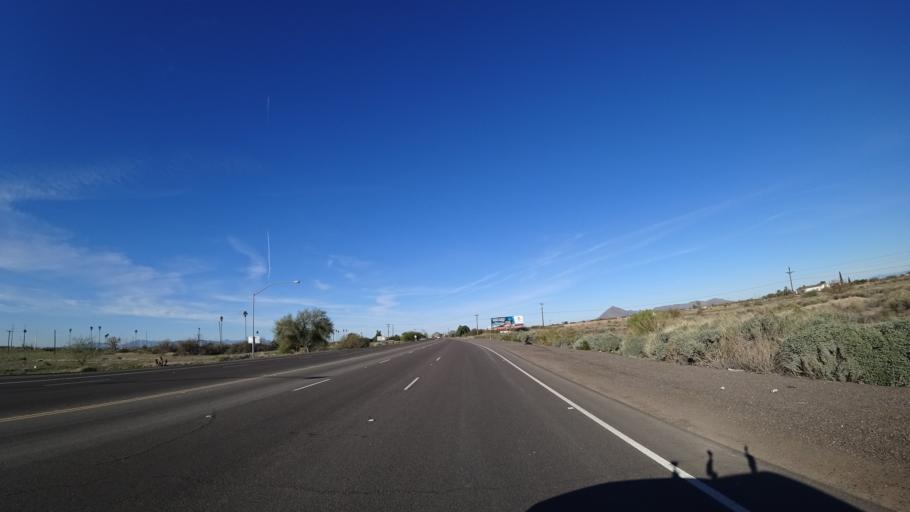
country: US
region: Arizona
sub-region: Maricopa County
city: Mesa
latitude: 33.4661
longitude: -111.8441
